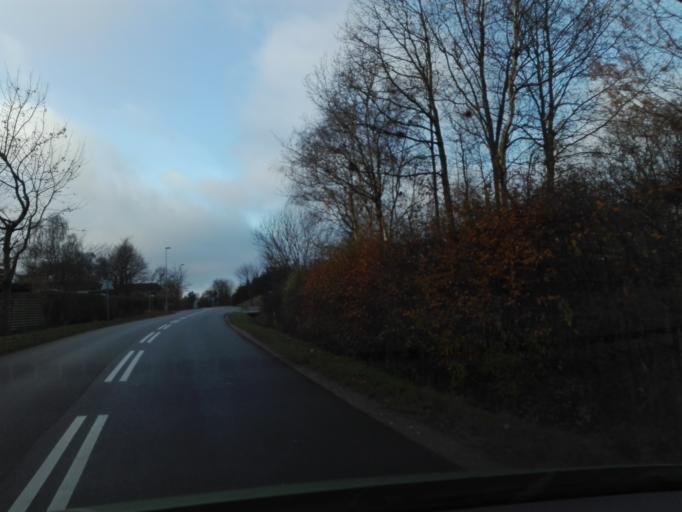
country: DK
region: Central Jutland
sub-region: Arhus Kommune
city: Solbjerg
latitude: 56.0322
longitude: 10.0396
